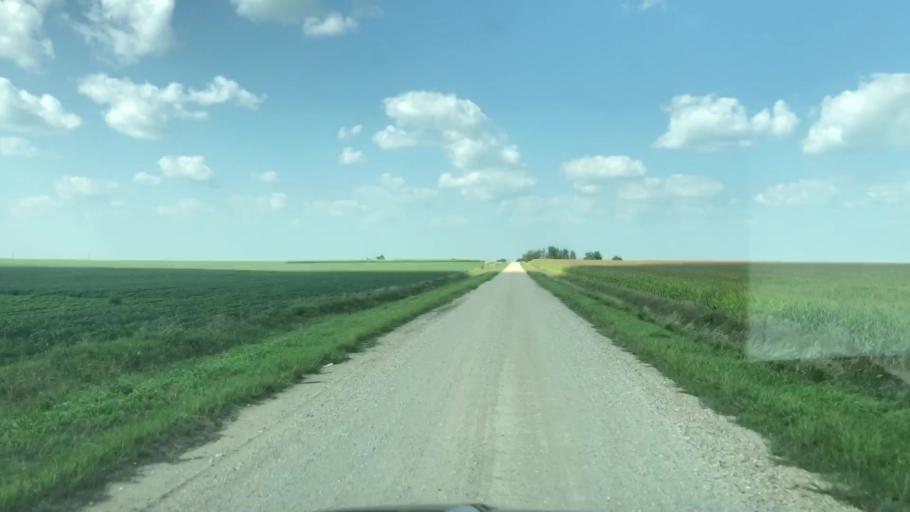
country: US
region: Iowa
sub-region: O'Brien County
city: Sheldon
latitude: 43.1786
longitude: -95.7824
